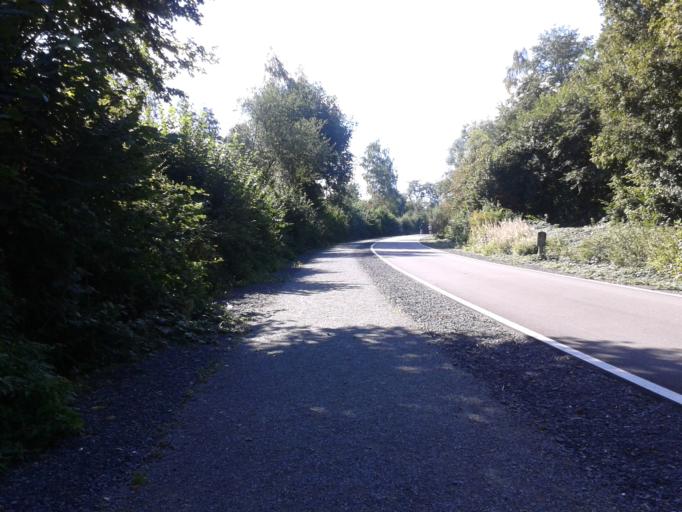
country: DE
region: North Rhine-Westphalia
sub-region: Regierungsbezirk Dusseldorf
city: Essen
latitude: 51.4503
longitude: 6.9501
